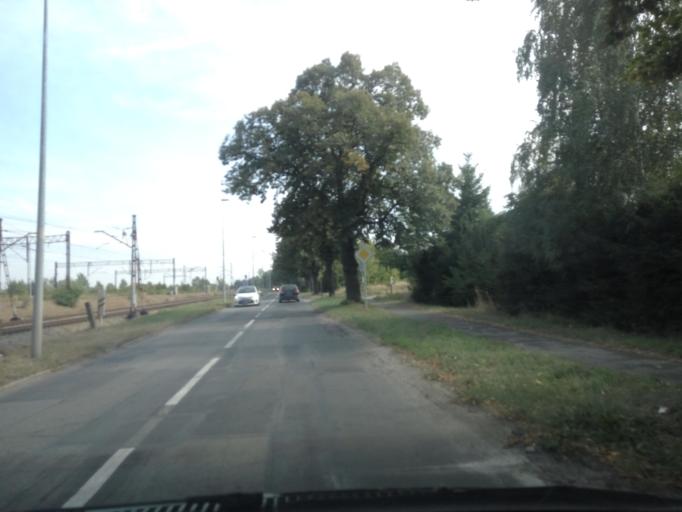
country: PL
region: Lower Silesian Voivodeship
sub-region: Powiat wroclawski
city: Radwanice
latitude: 51.0581
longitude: 17.0880
